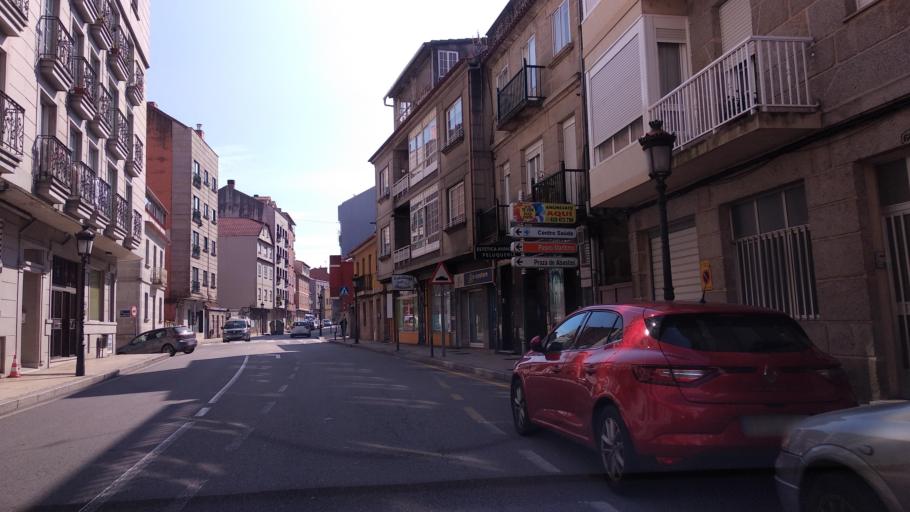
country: ES
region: Galicia
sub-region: Provincia de Pontevedra
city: Moana
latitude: 42.2836
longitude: -8.7355
